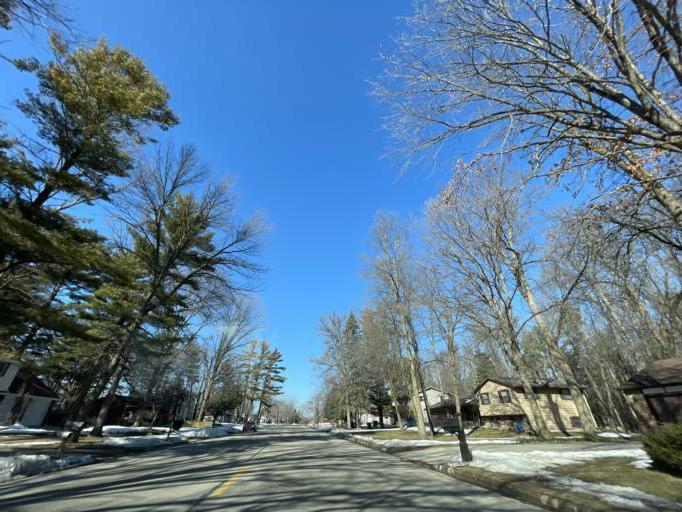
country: US
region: Wisconsin
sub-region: Brown County
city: Howard
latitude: 44.5695
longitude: -88.0803
